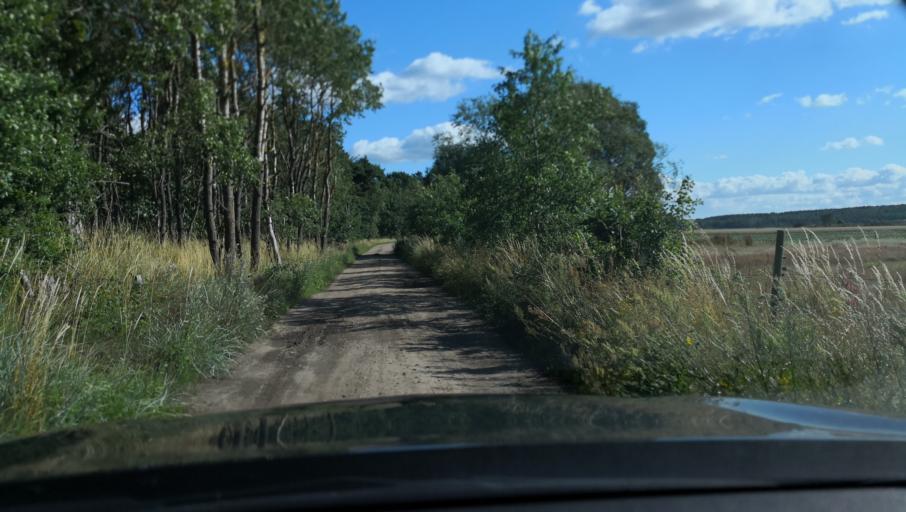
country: SE
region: Skane
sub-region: Kristianstads Kommun
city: Degeberga
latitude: 55.8050
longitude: 14.1969
